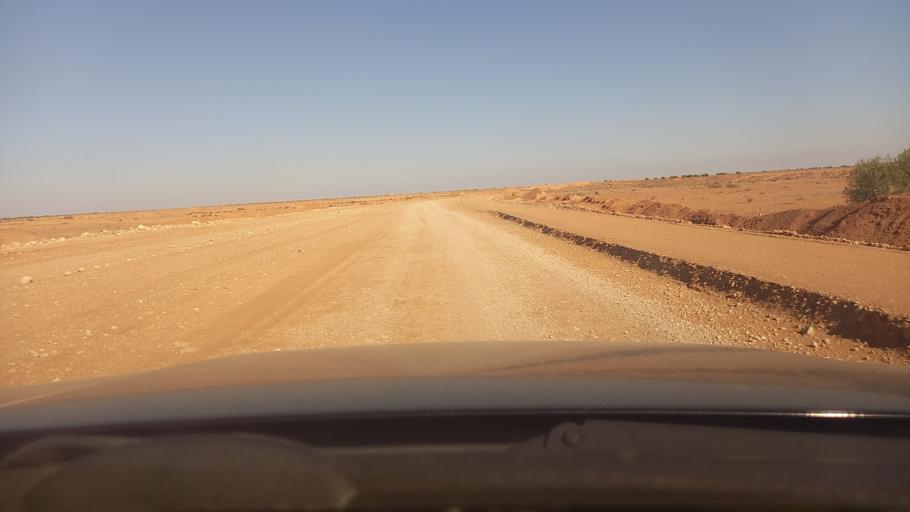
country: TN
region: Madanin
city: Medenine
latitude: 33.1444
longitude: 10.5064
